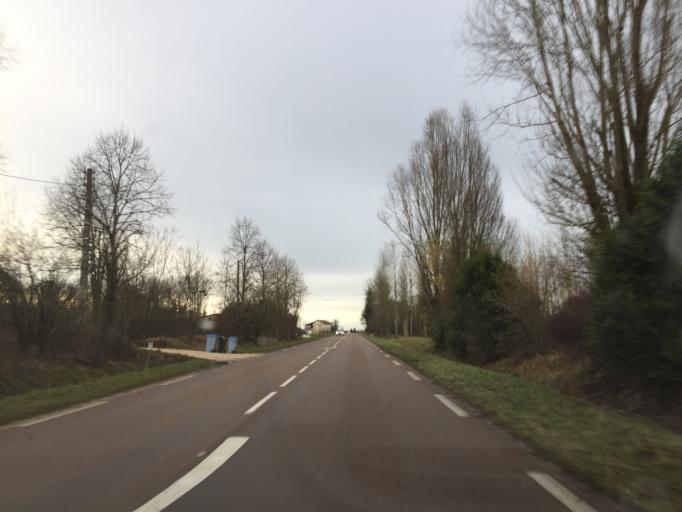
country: FR
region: Franche-Comte
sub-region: Departement du Jura
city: Choisey
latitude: 47.0596
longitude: 5.4940
